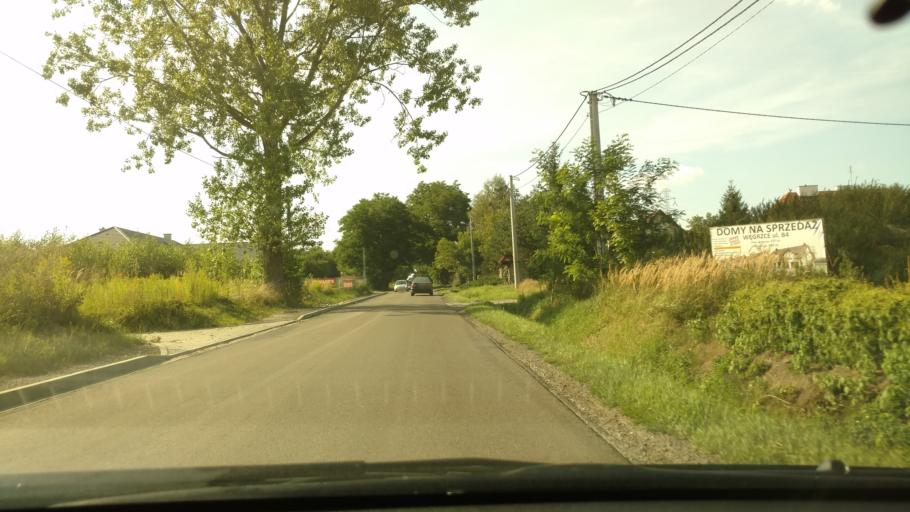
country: PL
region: Lesser Poland Voivodeship
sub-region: Powiat krakowski
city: Michalowice
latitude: 50.1077
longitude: 19.9826
